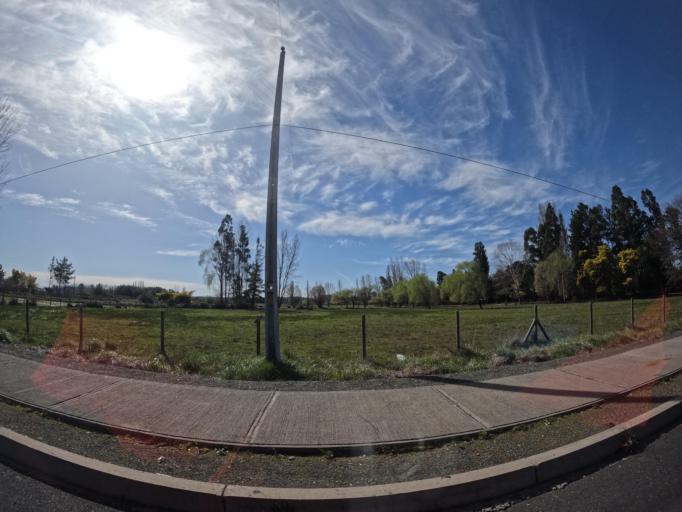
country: CL
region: Biobio
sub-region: Provincia de Biobio
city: Cabrero
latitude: -37.0246
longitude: -72.4557
